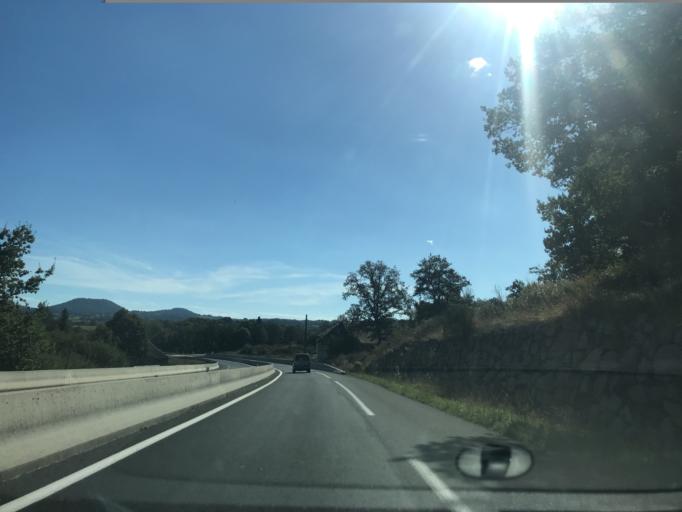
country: FR
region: Auvergne
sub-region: Departement du Puy-de-Dome
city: Gelles
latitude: 45.7374
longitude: 2.8614
